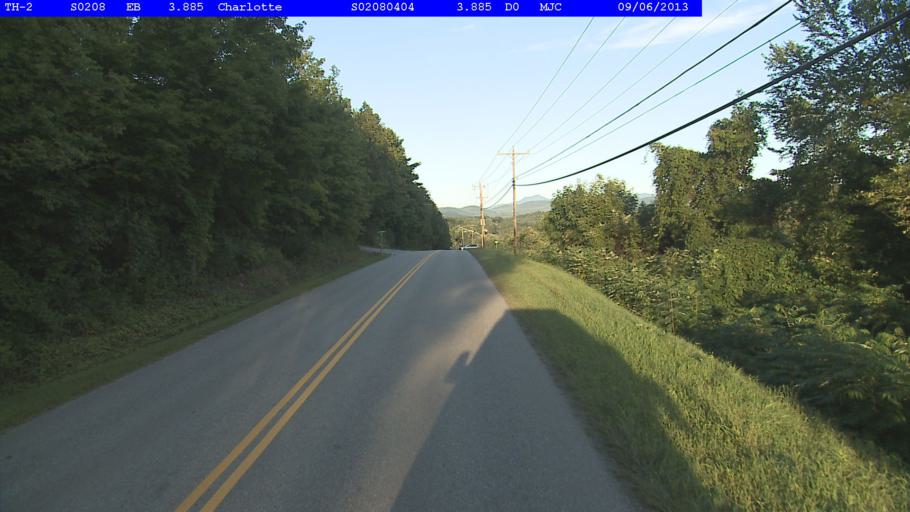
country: US
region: Vermont
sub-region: Chittenden County
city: Hinesburg
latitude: 44.3219
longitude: -73.1708
